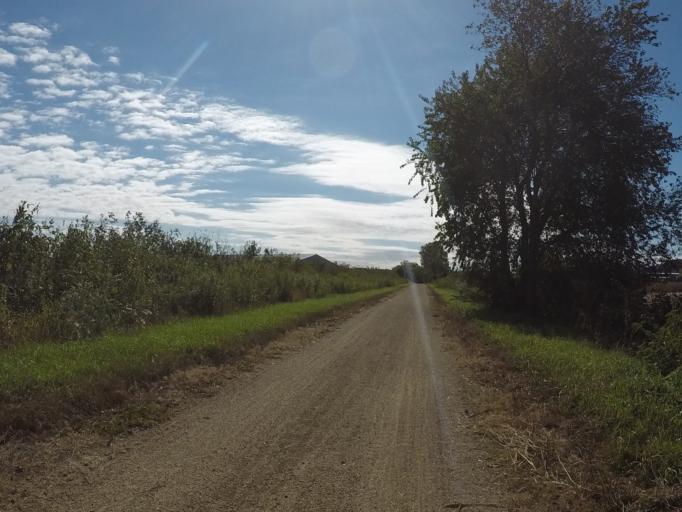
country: US
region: Wisconsin
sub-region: Richland County
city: Richland Center
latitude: 43.2948
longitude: -90.3296
